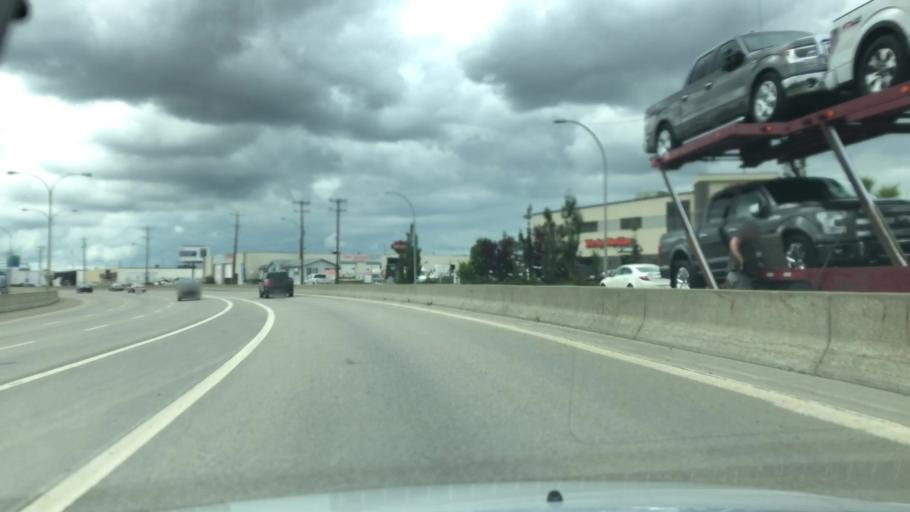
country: CA
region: Alberta
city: Edmonton
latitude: 53.5822
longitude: -113.4551
